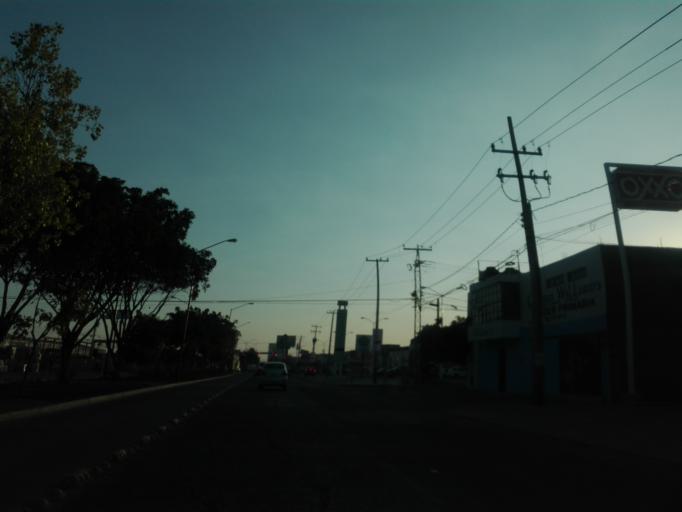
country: MX
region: Guanajuato
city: Leon
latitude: 21.1258
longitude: -101.6479
